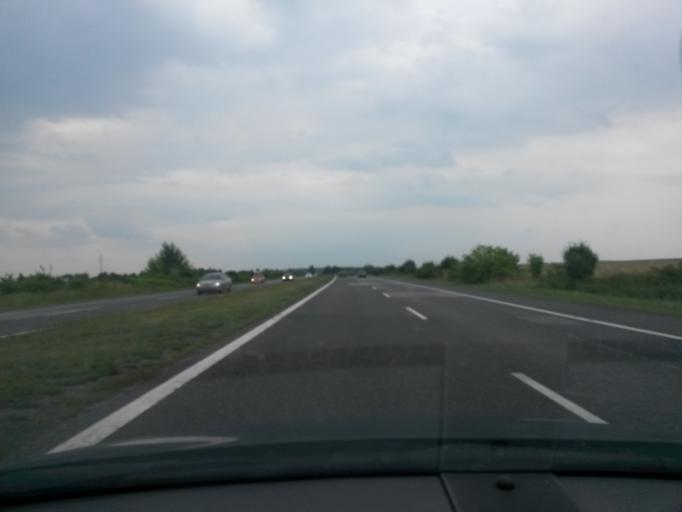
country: PL
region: Silesian Voivodeship
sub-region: Powiat czestochowski
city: Koscielec
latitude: 50.8787
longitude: 19.1634
